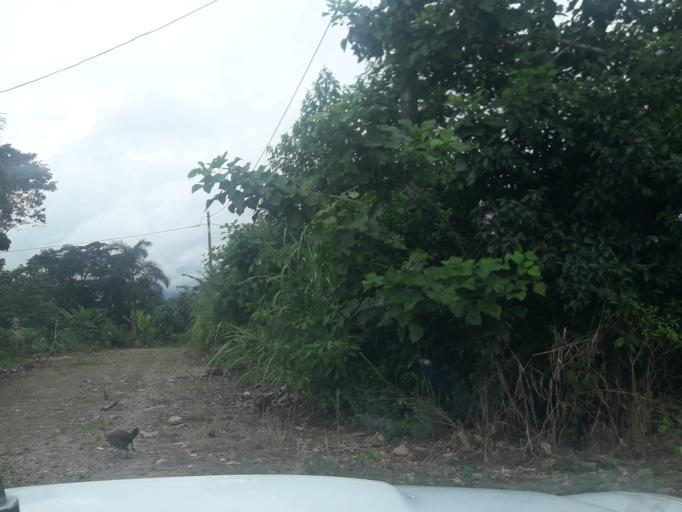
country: EC
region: Napo
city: Archidona
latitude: -0.9475
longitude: -77.8137
